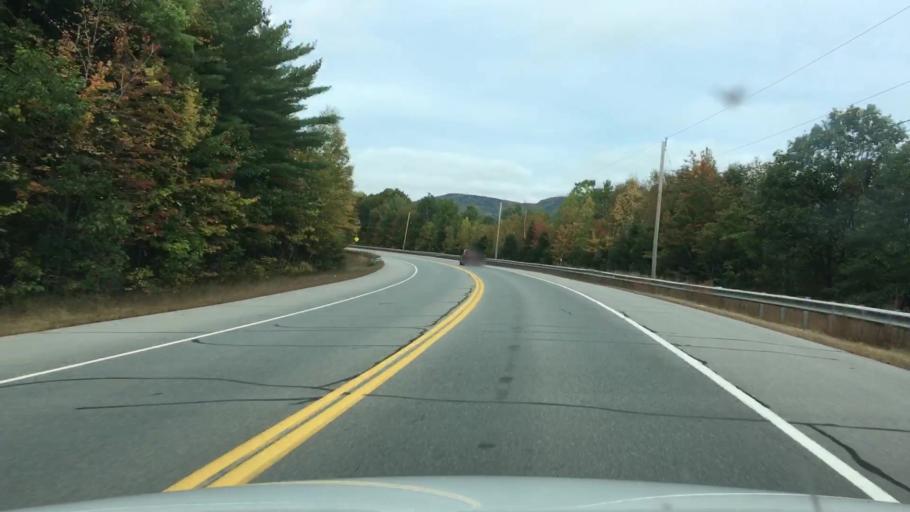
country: US
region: New Hampshire
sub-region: Coos County
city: Gorham
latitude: 44.3974
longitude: -71.0556
